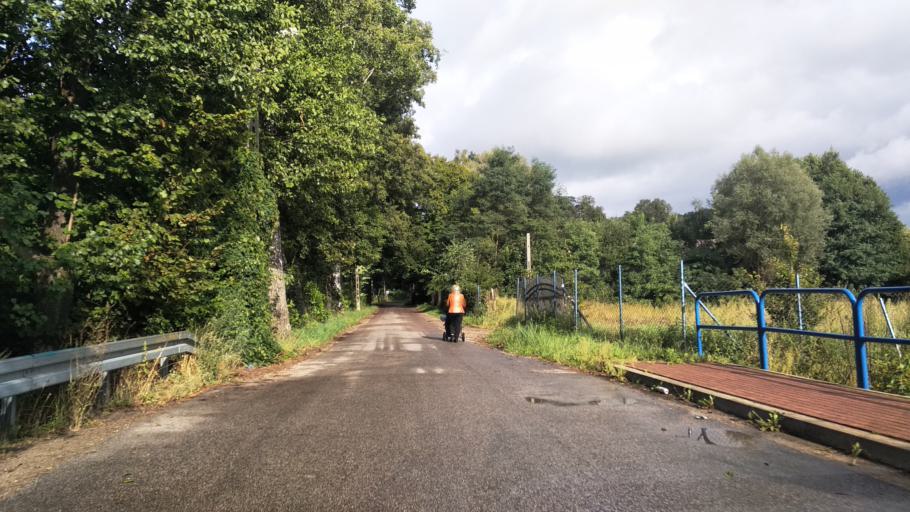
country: PL
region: Lodz Voivodeship
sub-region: Powiat lodzki wschodni
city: Andrespol
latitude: 51.7335
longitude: 19.6478
